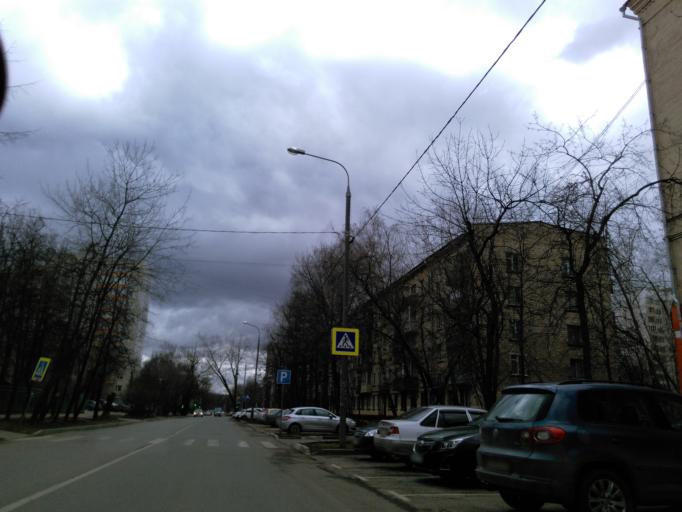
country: RU
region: Moskovskaya
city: Koptevo
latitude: 55.8358
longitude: 37.5266
